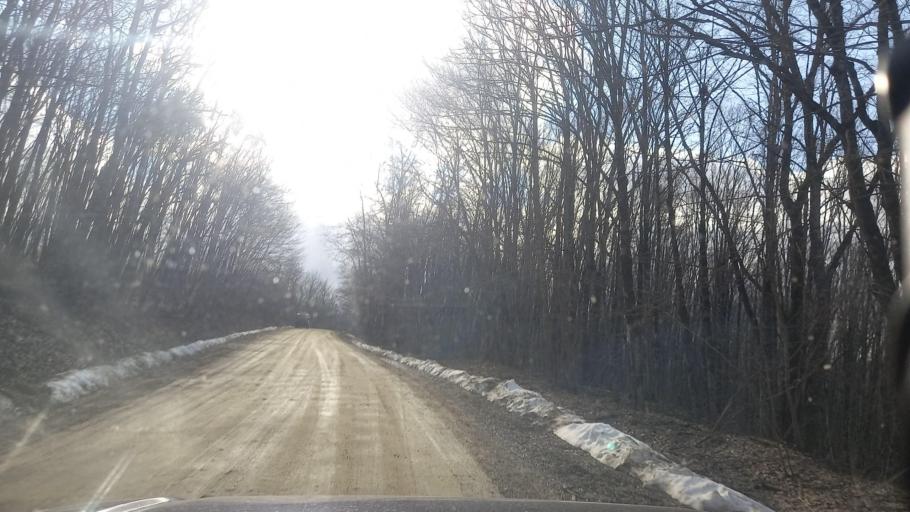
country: RU
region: Krasnodarskiy
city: Smolenskaya
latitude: 44.5862
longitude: 38.8124
